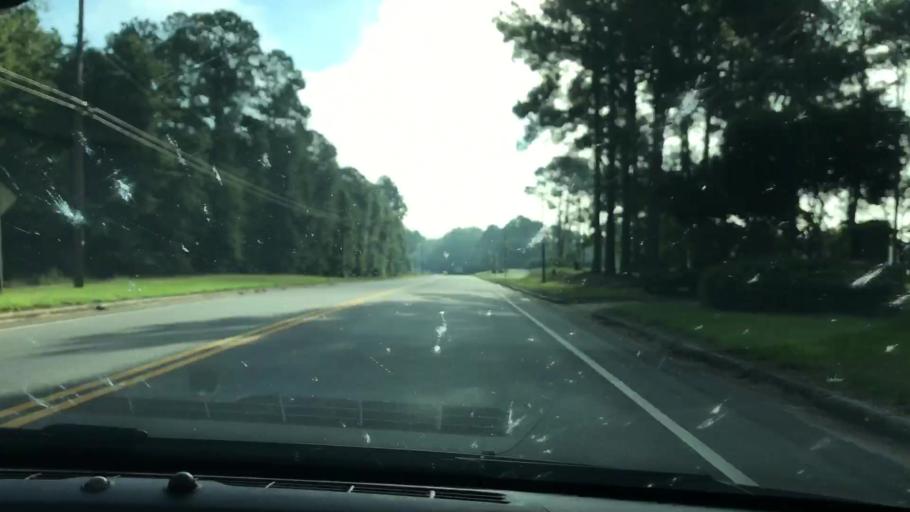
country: US
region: Georgia
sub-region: Terrell County
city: Dawson
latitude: 31.7692
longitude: -84.4614
